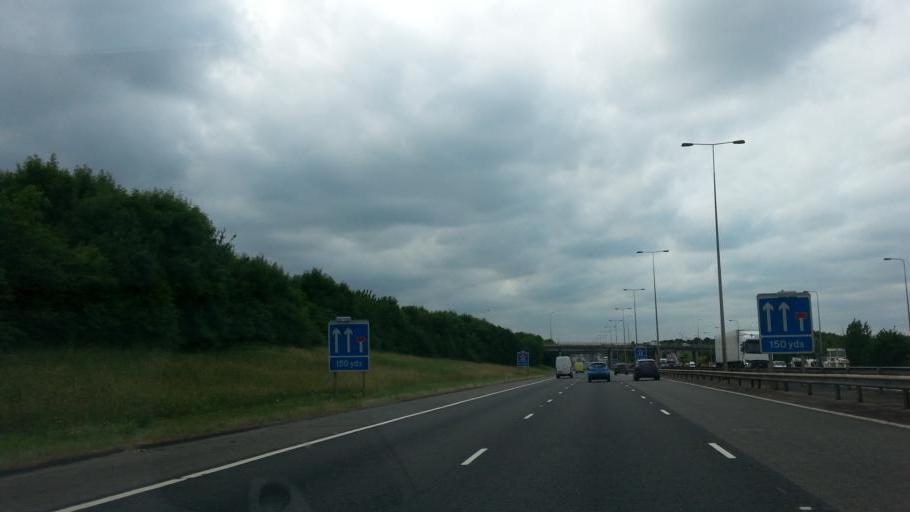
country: GB
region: England
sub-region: Cambridgeshire
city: Stilton
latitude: 52.5293
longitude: -0.3142
